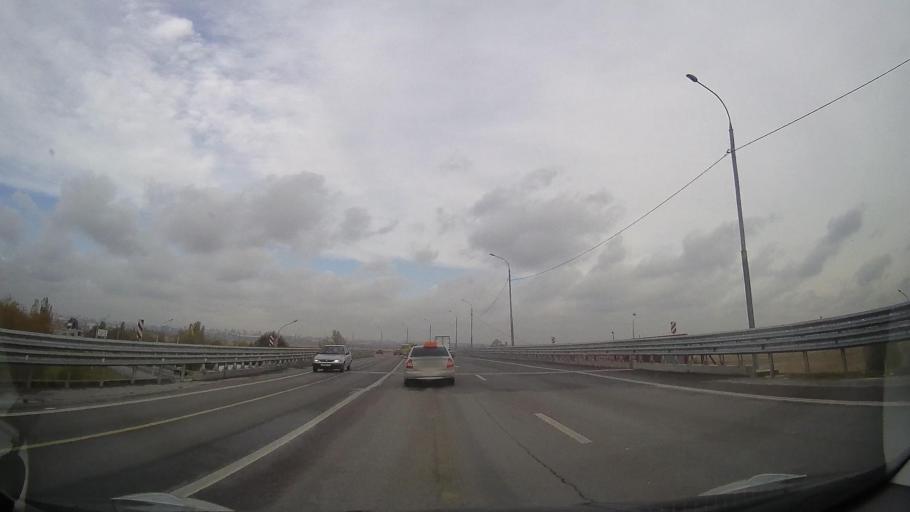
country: RU
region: Rostov
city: Bataysk
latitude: 47.1679
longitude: 39.7457
